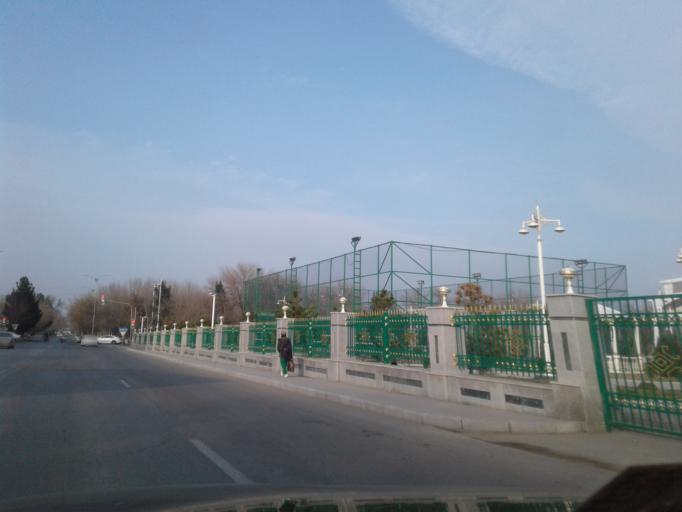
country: TM
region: Ahal
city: Ashgabat
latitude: 37.9446
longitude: 58.3606
